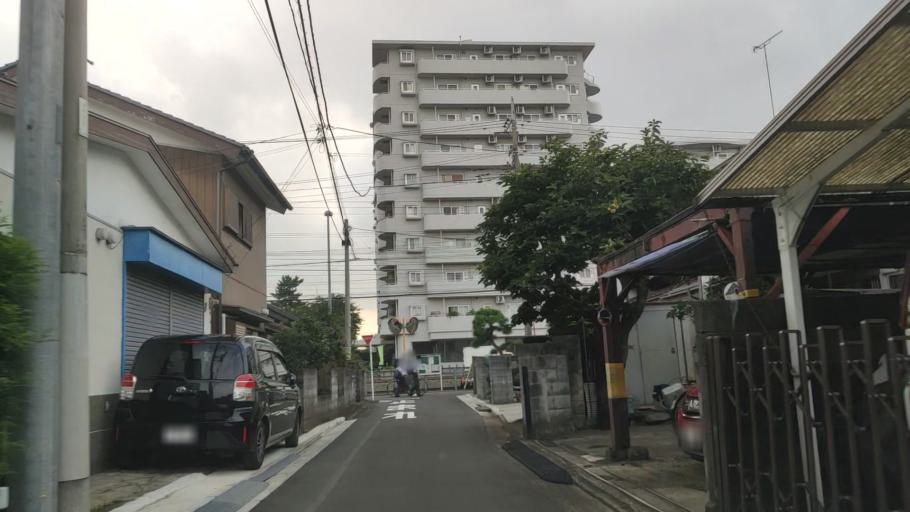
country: JP
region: Kanagawa
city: Minami-rinkan
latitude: 35.4874
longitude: 139.4528
